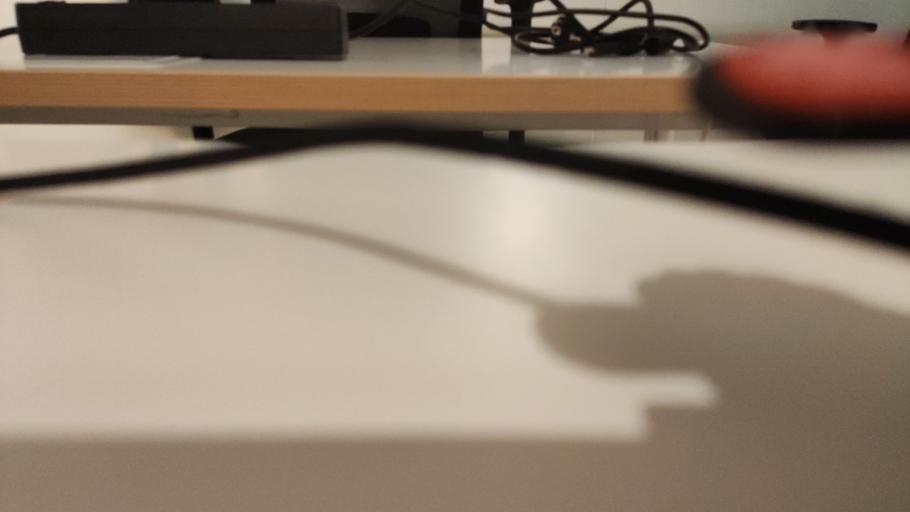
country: RU
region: Moskovskaya
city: Obolensk
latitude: 54.9930
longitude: 37.2765
